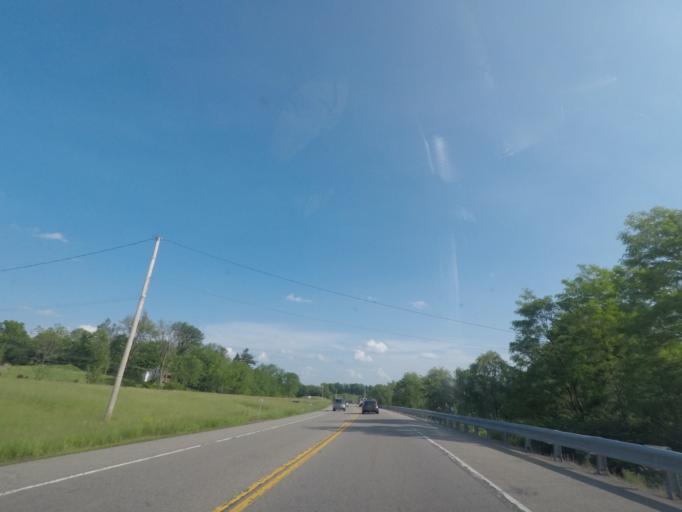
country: US
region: New York
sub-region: Orange County
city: Orange Lake
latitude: 41.5179
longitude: -74.1317
